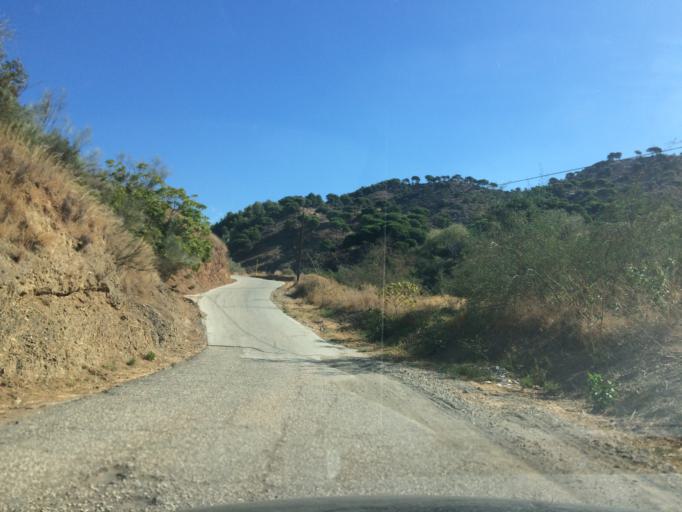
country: ES
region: Andalusia
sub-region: Provincia de Malaga
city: Malaga
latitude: 36.7615
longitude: -4.4230
